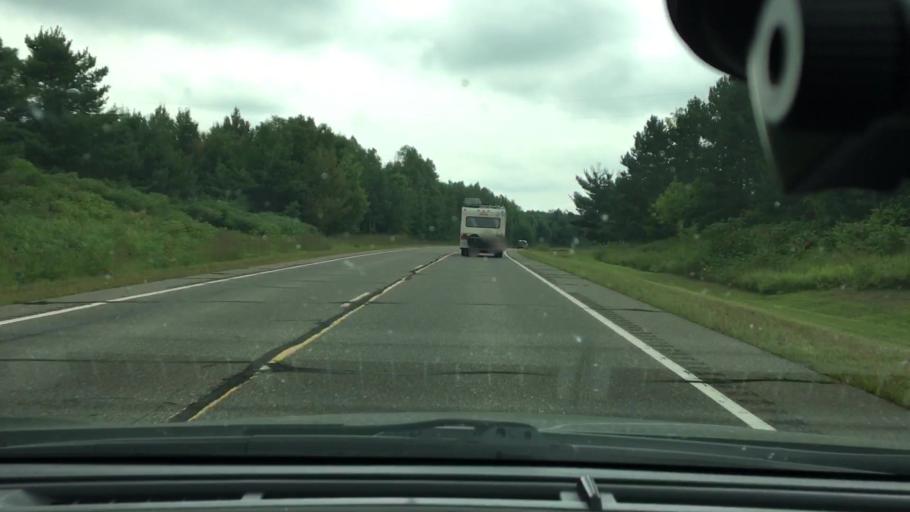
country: US
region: Minnesota
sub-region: Crow Wing County
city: Crosby
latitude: 46.4369
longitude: -93.8746
